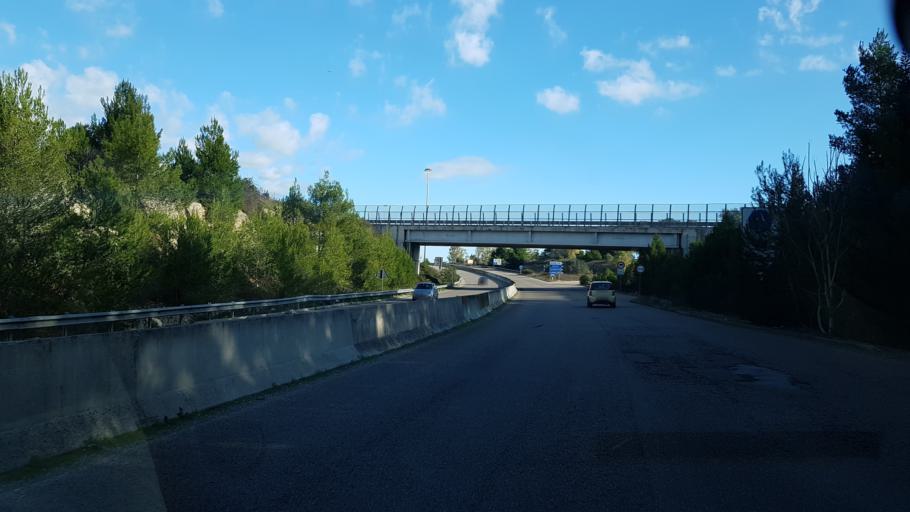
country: IT
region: Apulia
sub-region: Provincia di Lecce
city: Castromediano
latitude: 40.3235
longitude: 18.1885
